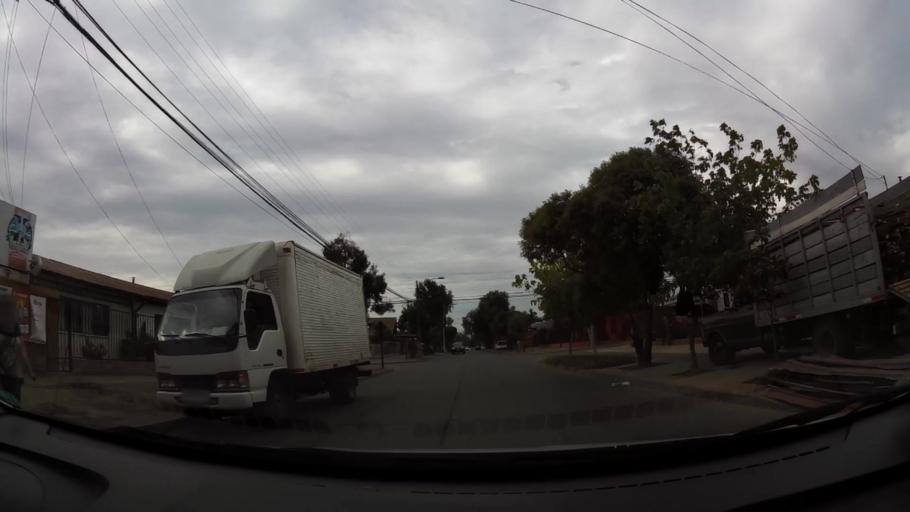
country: CL
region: O'Higgins
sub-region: Provincia de Cachapoal
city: Rancagua
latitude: -34.1605
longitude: -70.7481
